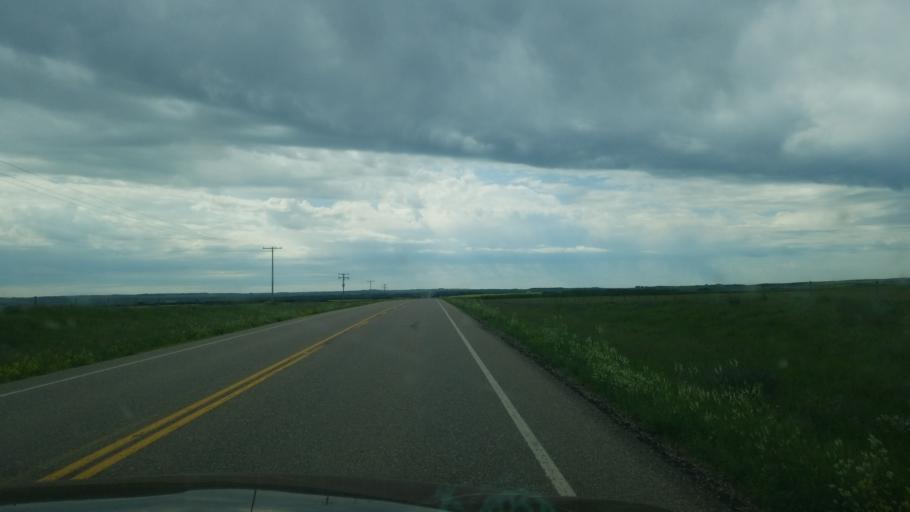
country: CA
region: Saskatchewan
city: Unity
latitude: 52.9693
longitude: -109.3426
